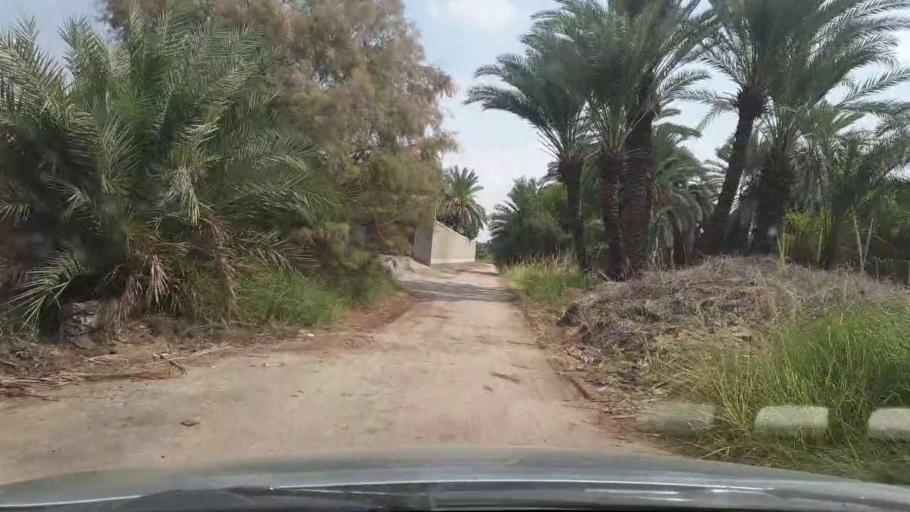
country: PK
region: Sindh
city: Khairpur
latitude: 27.4666
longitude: 68.7765
